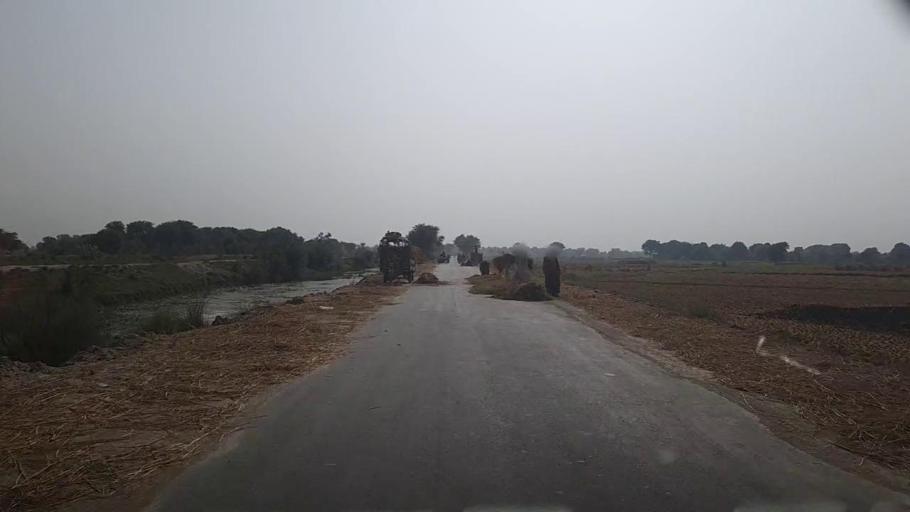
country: PK
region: Sindh
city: Kashmor
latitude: 28.4171
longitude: 69.5687
